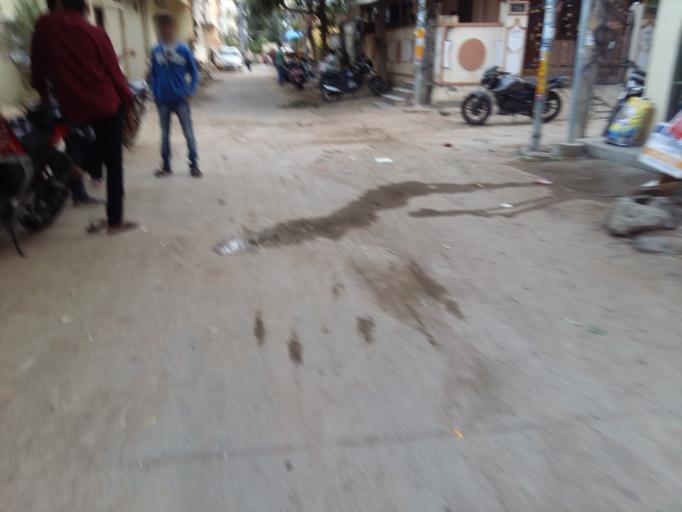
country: IN
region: Telangana
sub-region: Rangareddi
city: Kukatpalli
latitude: 17.4876
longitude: 78.3974
